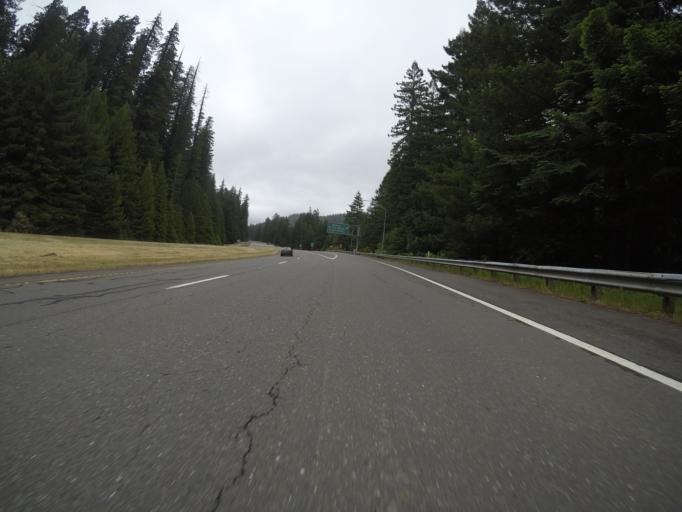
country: US
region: California
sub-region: Humboldt County
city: Rio Dell
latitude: 40.4399
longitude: -124.0357
